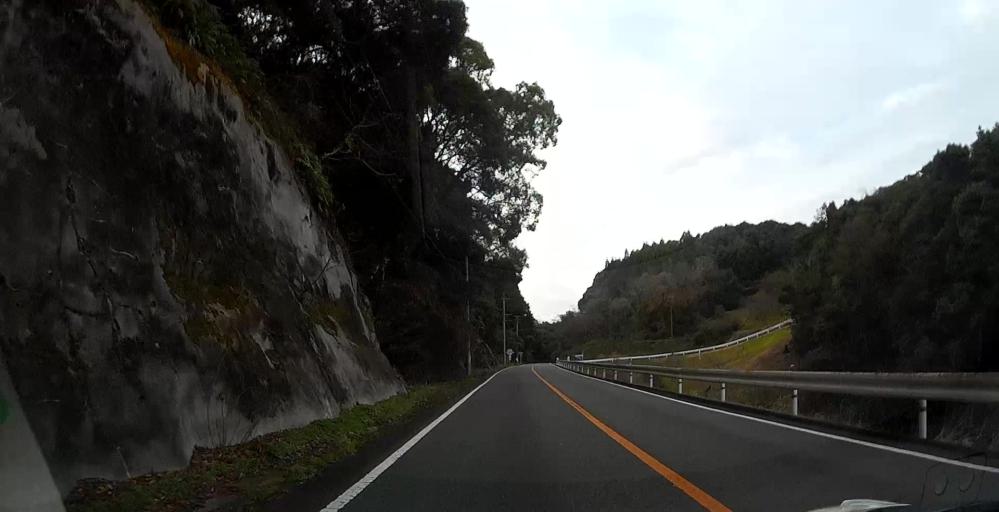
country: JP
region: Kumamoto
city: Hondo
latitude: 32.5050
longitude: 130.3881
